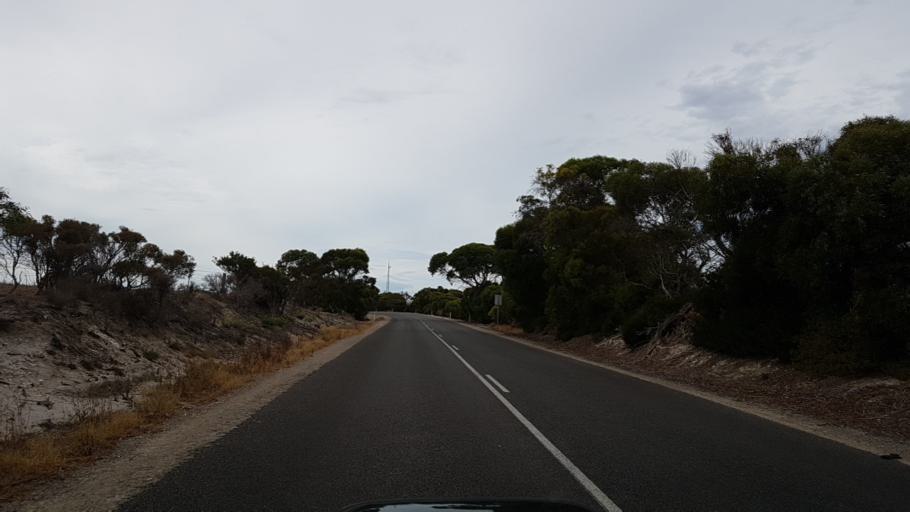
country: AU
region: South Australia
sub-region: Yorke Peninsula
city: Honiton
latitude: -34.9867
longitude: 137.1253
